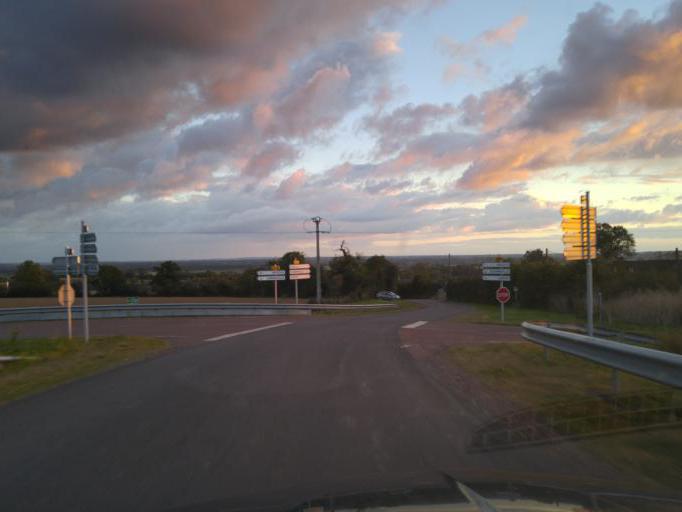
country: FR
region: Lower Normandy
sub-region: Departement du Calvados
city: Grandcamp-Maisy
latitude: 49.3406
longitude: -0.9803
